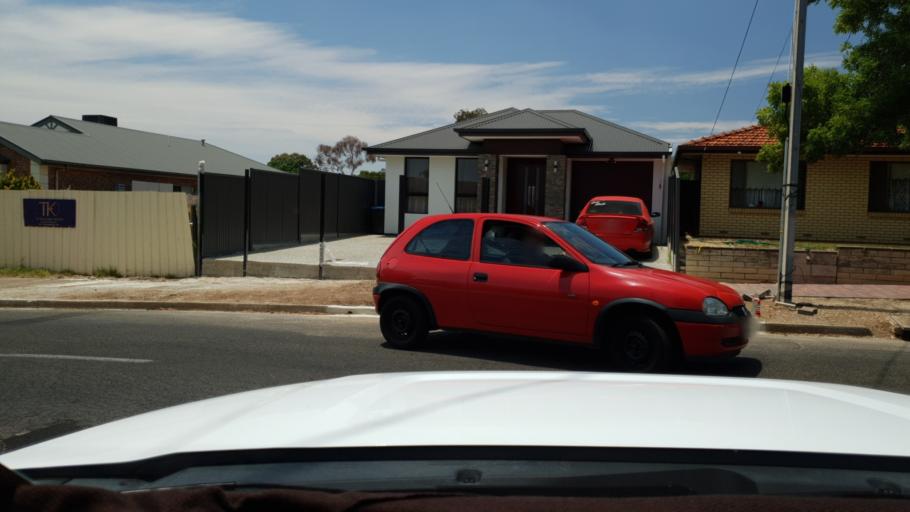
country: AU
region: South Australia
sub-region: Marion
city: Clovelly Park
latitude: -35.0029
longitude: 138.5824
